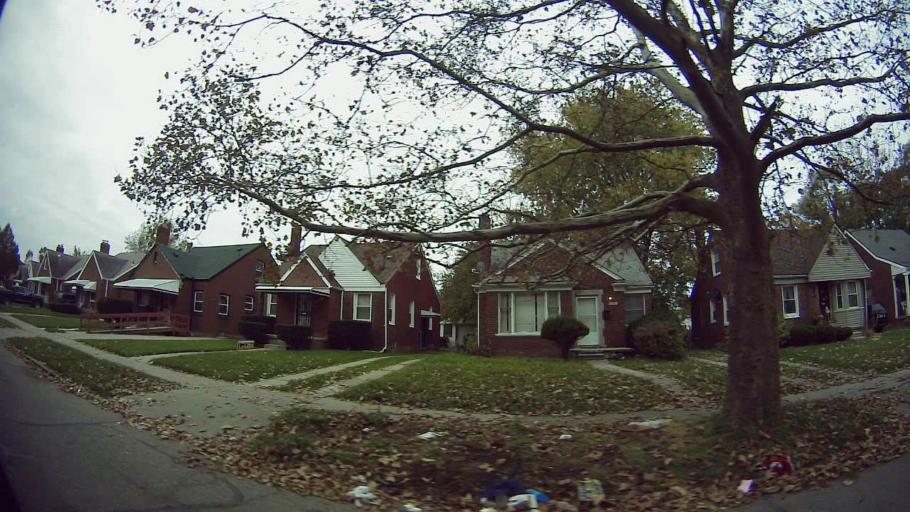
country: US
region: Michigan
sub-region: Wayne County
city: Dearborn
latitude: 42.3718
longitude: -83.1877
